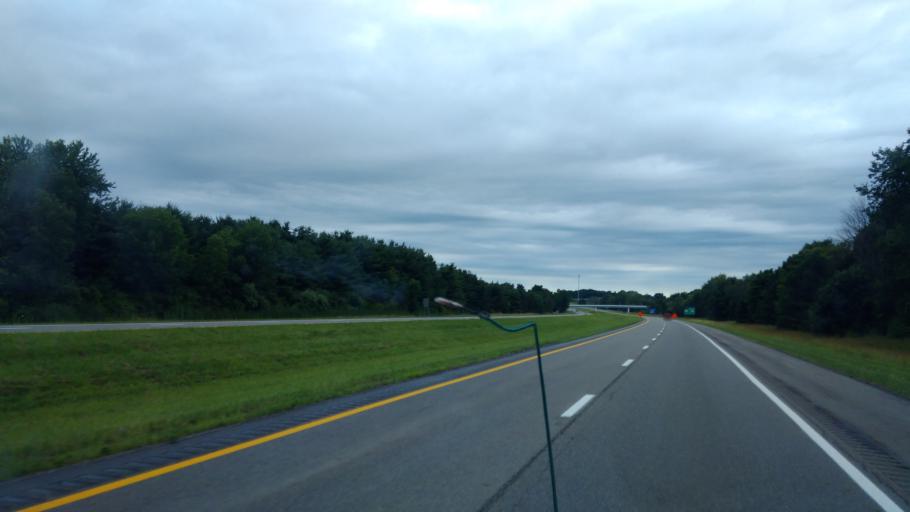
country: US
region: Ohio
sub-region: Columbiana County
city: Columbiana
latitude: 40.9082
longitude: -80.7208
